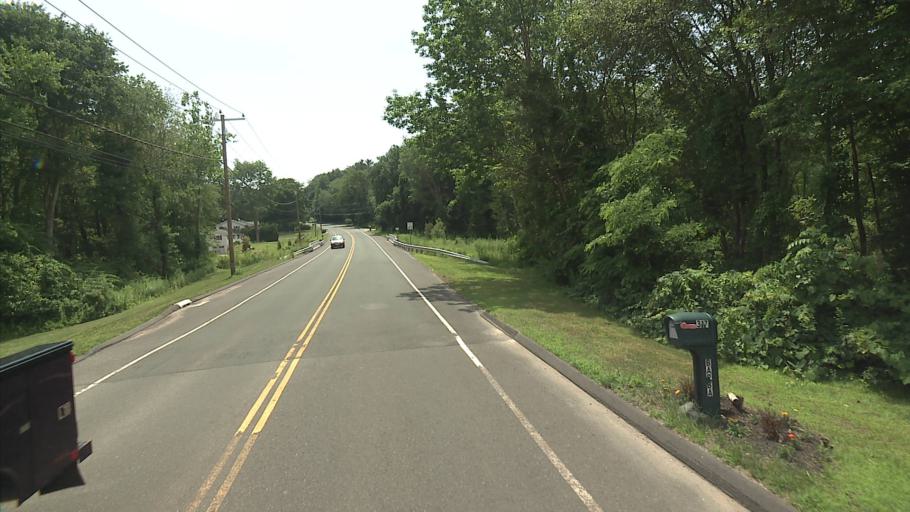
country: US
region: Connecticut
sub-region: New Haven County
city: Madison
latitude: 41.3052
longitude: -72.5908
